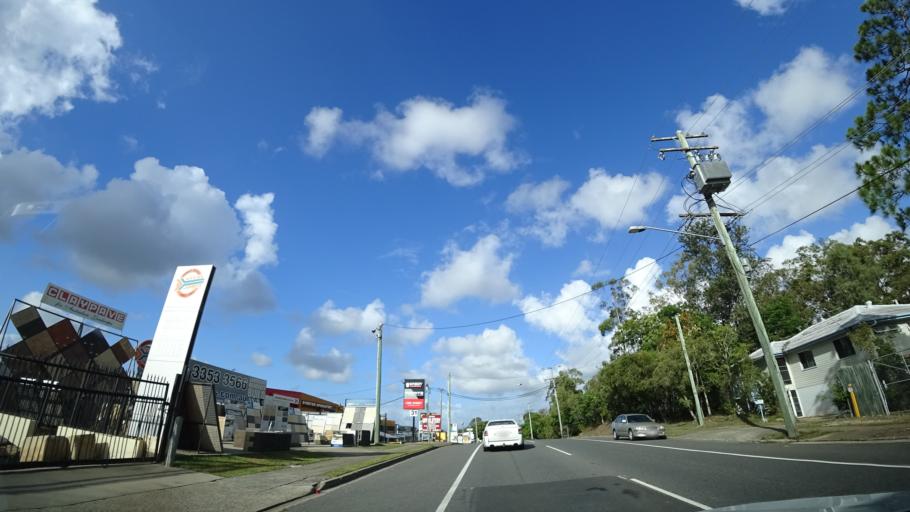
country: AU
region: Queensland
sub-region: Brisbane
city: Everton Park
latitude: -27.3896
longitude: 152.9772
